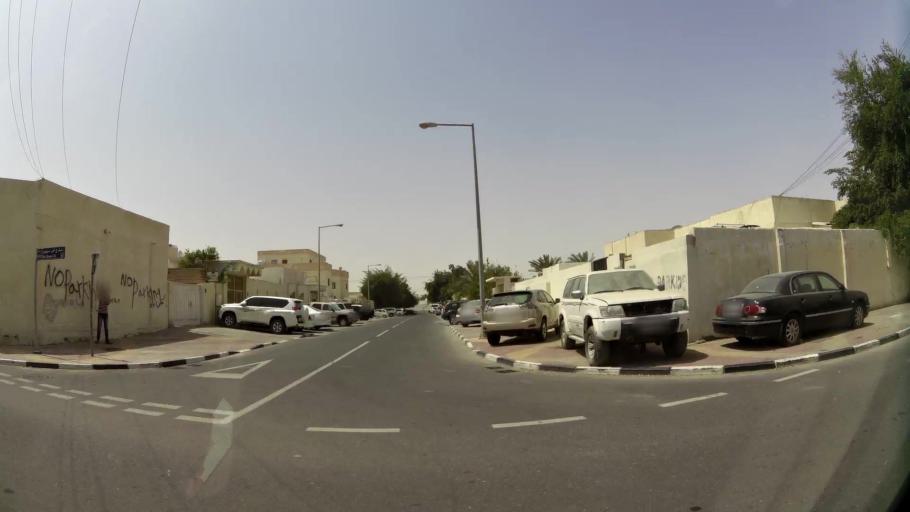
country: QA
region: Baladiyat ad Dawhah
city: Doha
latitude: 25.3164
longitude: 51.4809
